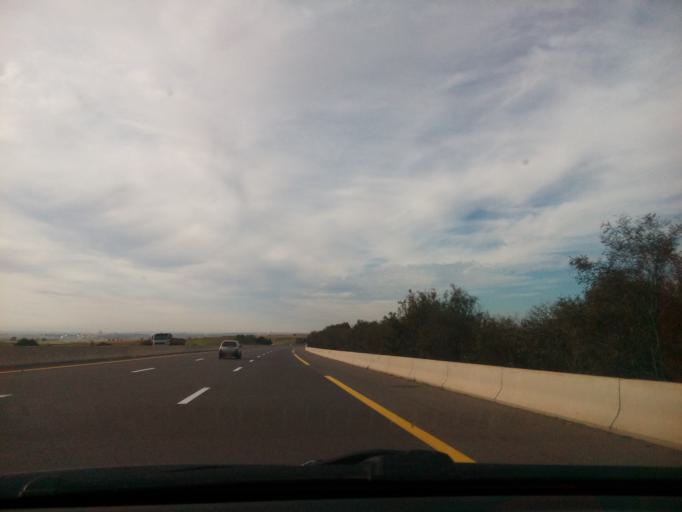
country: DZ
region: Sidi Bel Abbes
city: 'Ain el Berd
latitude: 35.3318
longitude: -0.5252
